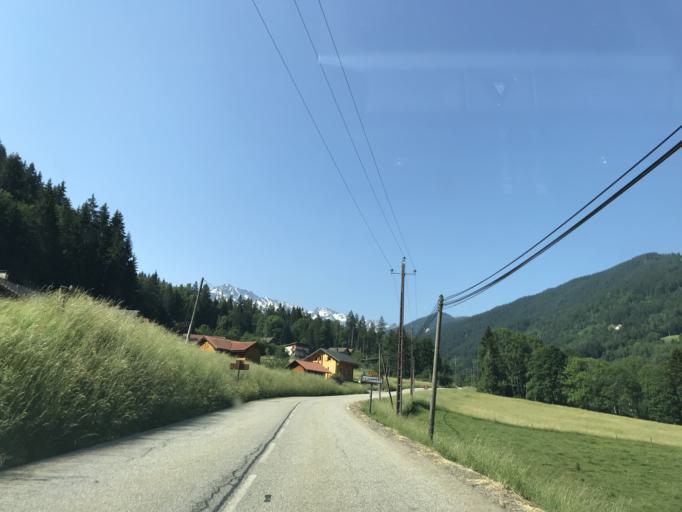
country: FR
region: Rhone-Alpes
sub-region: Departement de l'Isere
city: Allevard
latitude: 45.3170
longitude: 6.0864
